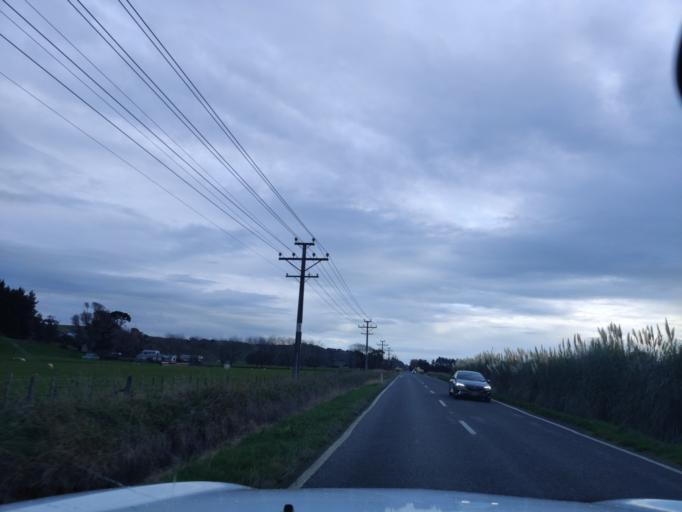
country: NZ
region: Manawatu-Wanganui
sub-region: Palmerston North City
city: Palmerston North
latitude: -40.3547
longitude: 175.6898
